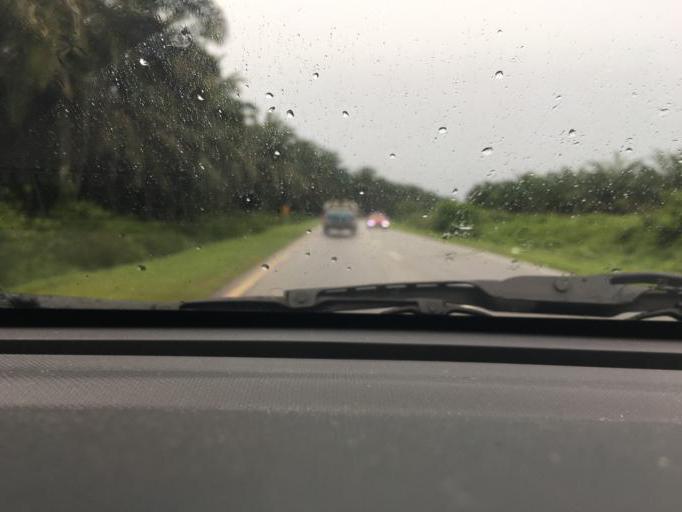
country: MY
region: Kedah
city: Bedong
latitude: 5.6552
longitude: 100.6328
